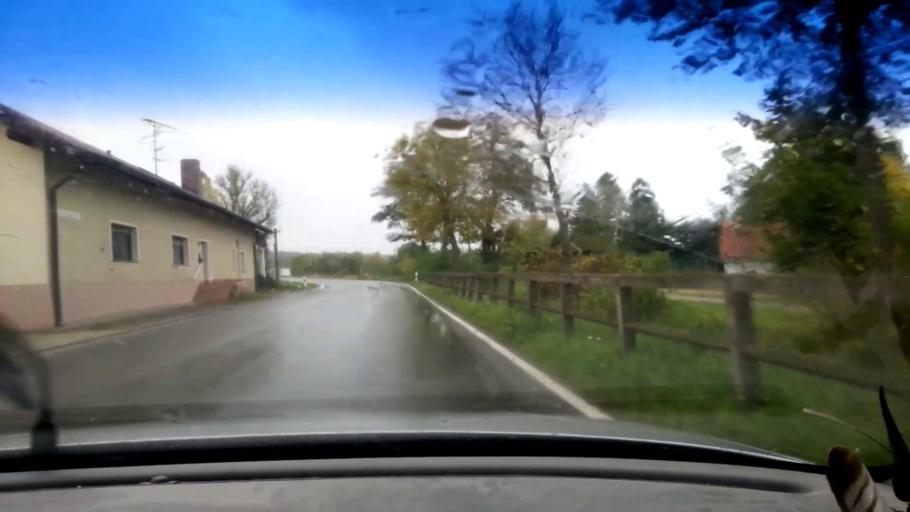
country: DE
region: Bavaria
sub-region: Upper Franconia
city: Walsdorf
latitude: 49.8701
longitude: 10.7783
